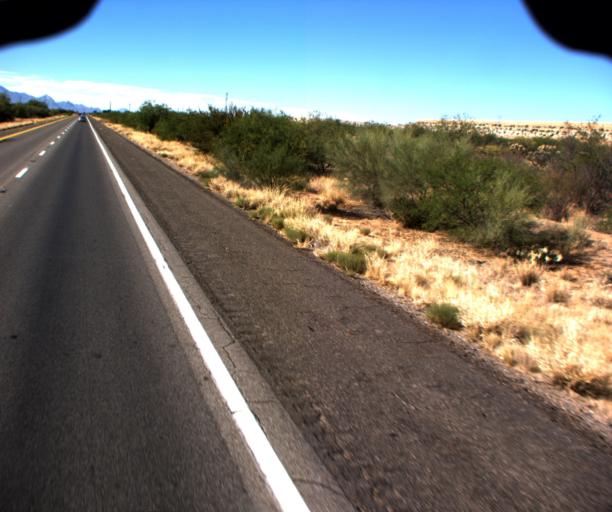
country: US
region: Arizona
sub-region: Pima County
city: Sahuarita
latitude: 31.9808
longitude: -110.9910
